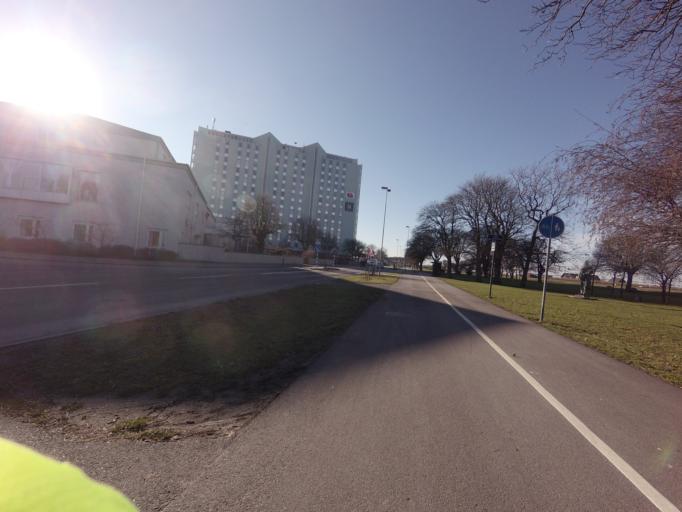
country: SE
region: Skane
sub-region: Malmo
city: Bunkeflostrand
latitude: 55.5831
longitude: 12.9221
